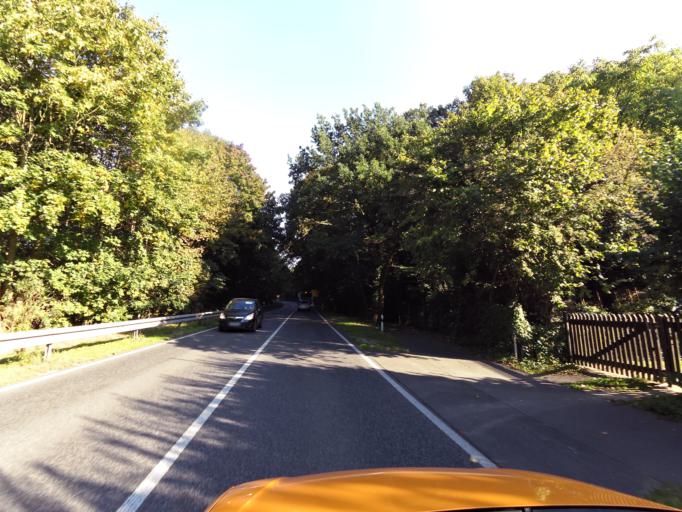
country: DE
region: Brandenburg
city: Potsdam
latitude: 52.4599
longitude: 13.0563
